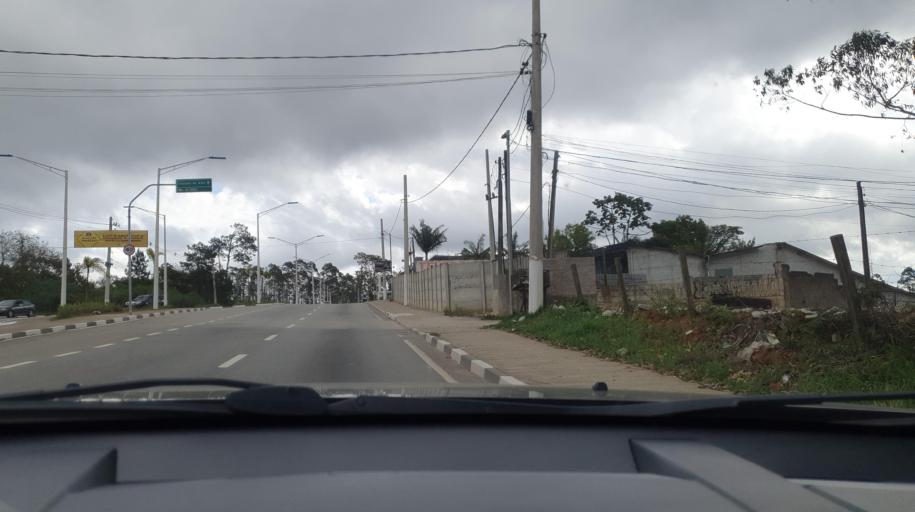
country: BR
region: Sao Paulo
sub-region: Vargem Grande Paulista
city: Vargem Grande Paulista
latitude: -23.6703
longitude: -47.0122
